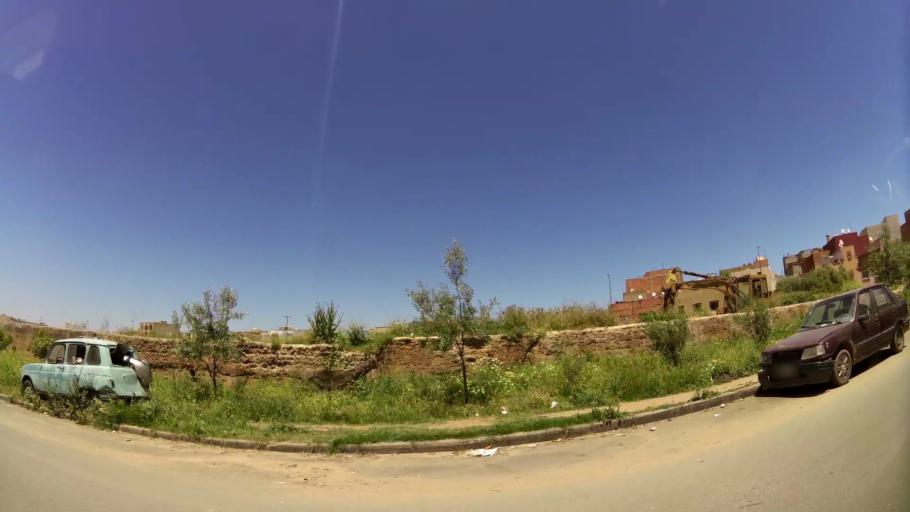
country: MA
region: Meknes-Tafilalet
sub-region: Meknes
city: Meknes
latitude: 33.8637
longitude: -5.5702
